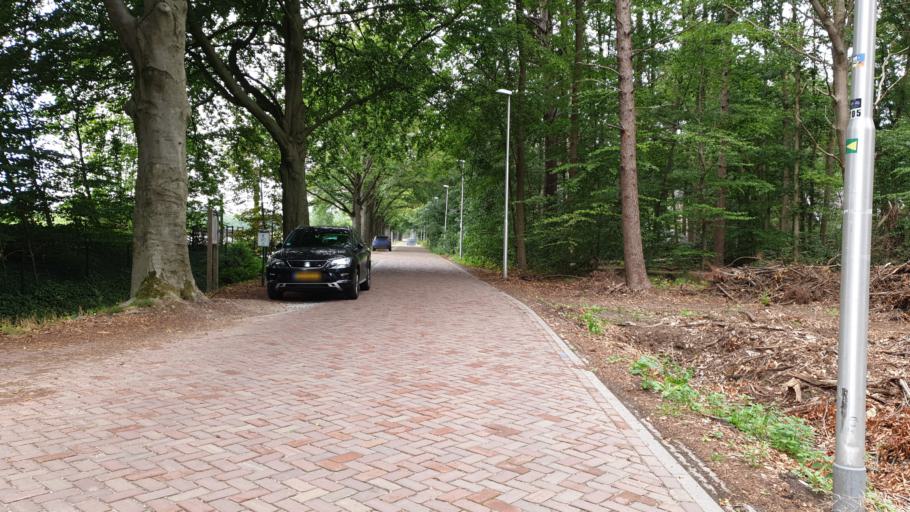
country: NL
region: North Brabant
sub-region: Gemeente Eindhoven
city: Meerhoven
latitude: 51.4628
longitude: 5.4273
